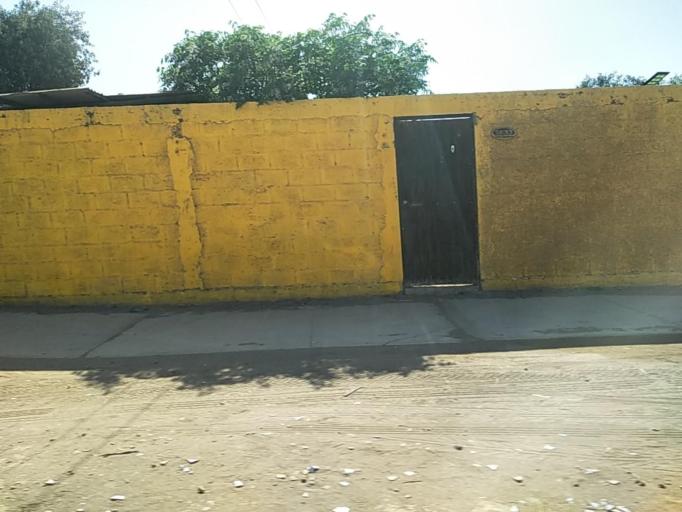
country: CL
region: Atacama
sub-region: Provincia de Copiapo
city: Copiapo
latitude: -27.4049
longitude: -70.2895
